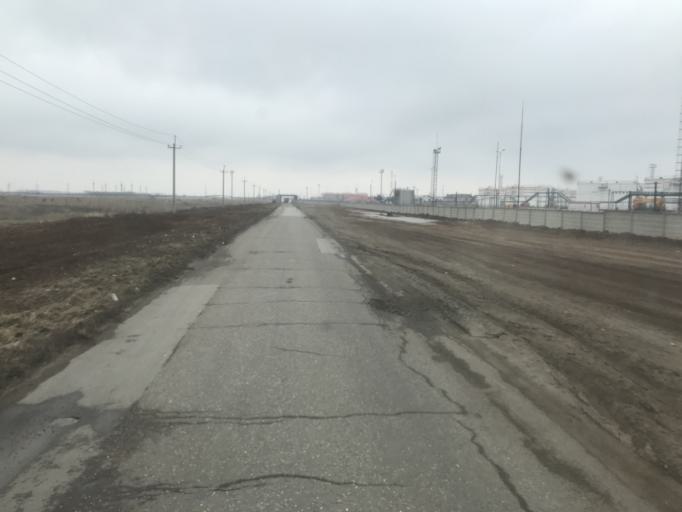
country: RU
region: Volgograd
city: Svetlyy Yar
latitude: 48.5055
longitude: 44.6447
